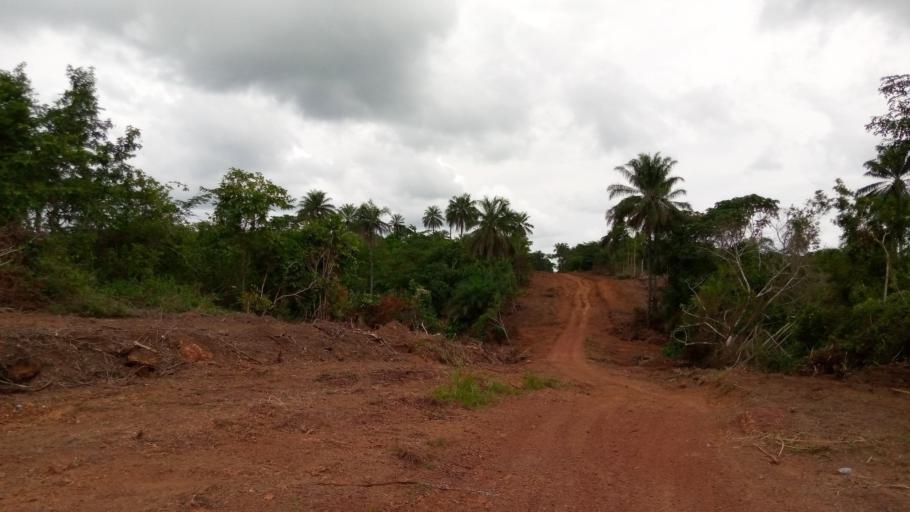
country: SL
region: Southern Province
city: Moyamba
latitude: 8.1948
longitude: -12.5380
